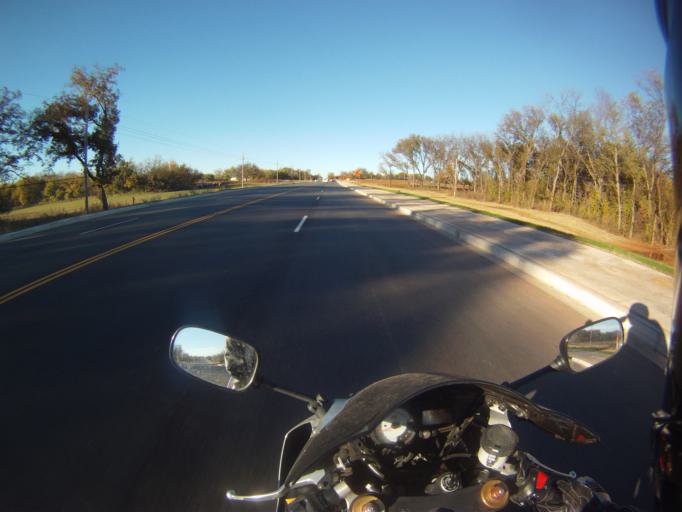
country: US
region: Oklahoma
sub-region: Payne County
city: Stillwater
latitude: 36.1264
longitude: -97.1230
